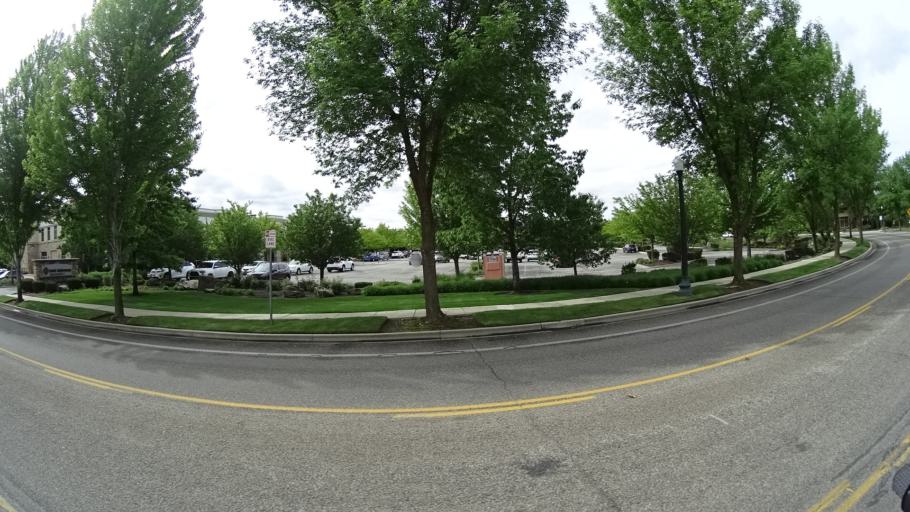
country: US
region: Idaho
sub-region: Ada County
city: Eagle
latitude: 43.6897
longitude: -116.3510
